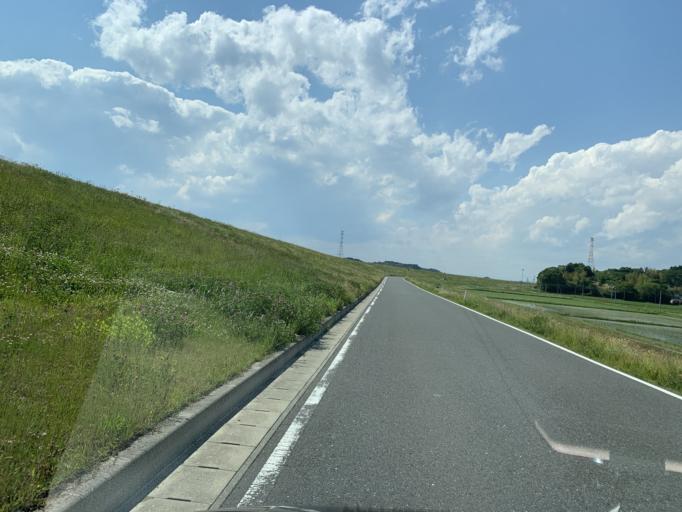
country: JP
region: Miyagi
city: Matsushima
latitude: 38.4230
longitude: 141.1300
